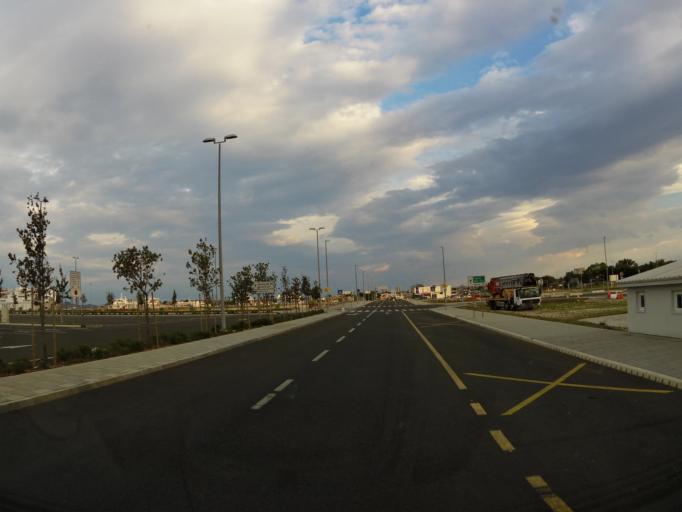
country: HR
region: Zadarska
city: Zadar
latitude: 44.0917
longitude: 15.2618
